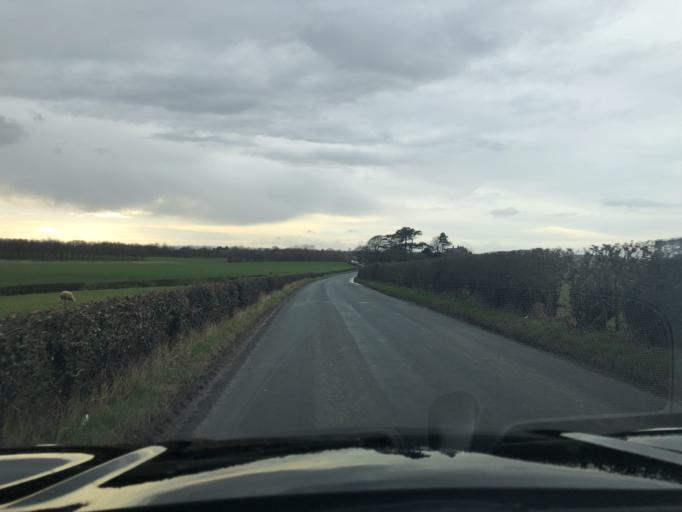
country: GB
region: England
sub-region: North Yorkshire
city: Northallerton
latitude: 54.3425
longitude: -1.4567
